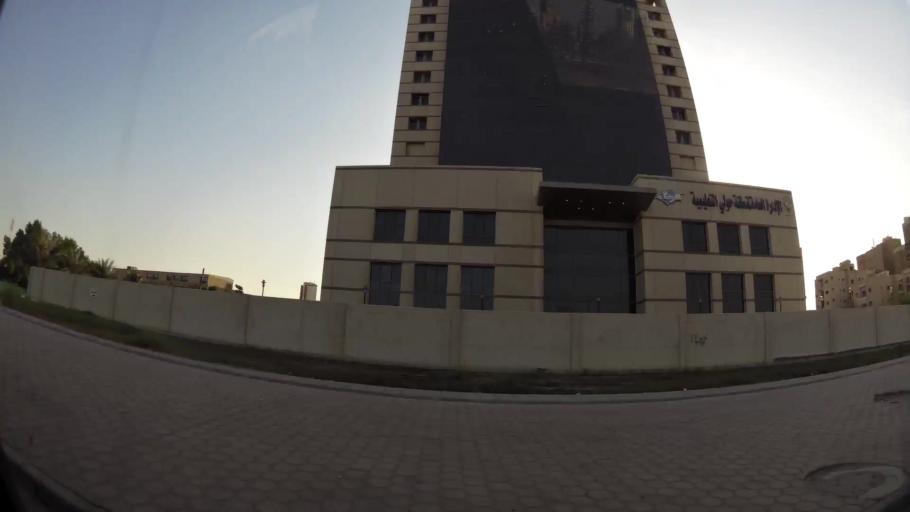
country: KW
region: Muhafazat Hawalli
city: As Salimiyah
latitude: 29.3298
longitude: 48.0731
